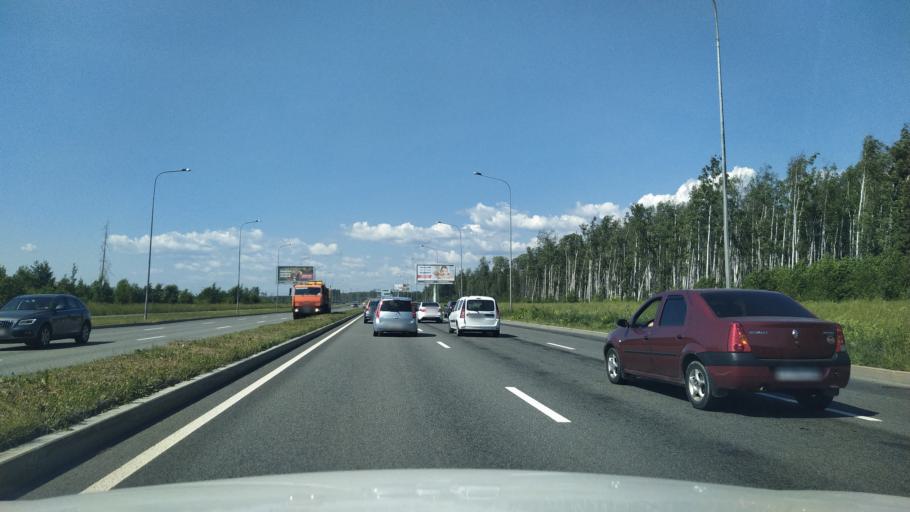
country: RU
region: St.-Petersburg
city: Levashovo
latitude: 60.0674
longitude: 30.1893
